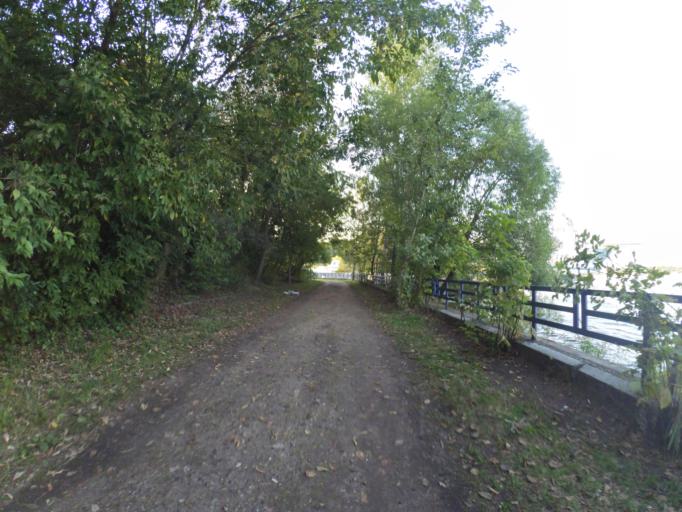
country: RU
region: Moskovskaya
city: Levoberezhnyy
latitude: 55.8507
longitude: 37.4560
